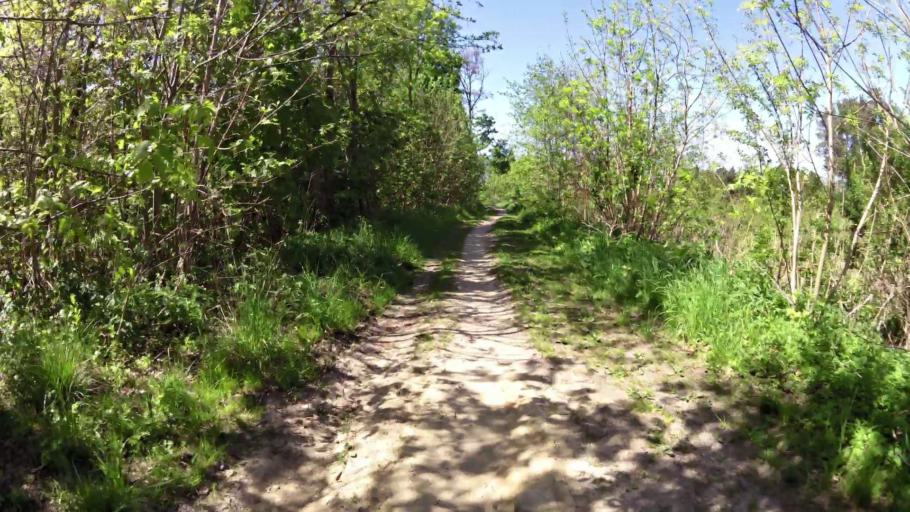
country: PL
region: West Pomeranian Voivodeship
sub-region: Powiat bialogardzki
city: Bialogard
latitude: 53.9998
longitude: 16.0272
